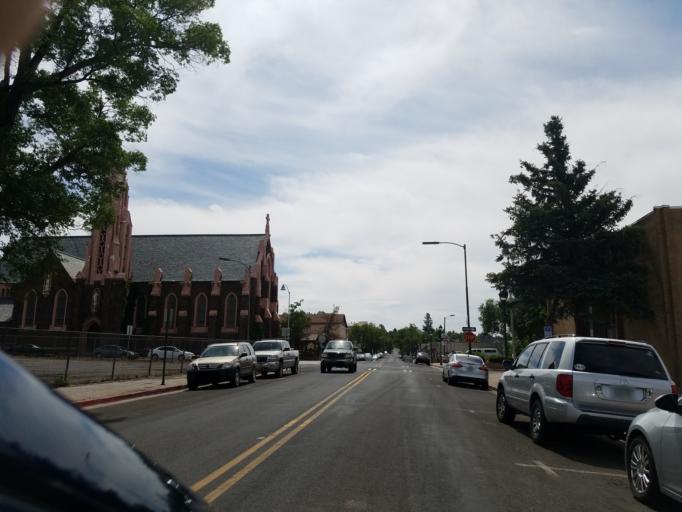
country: US
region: Arizona
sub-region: Coconino County
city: Flagstaff
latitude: 35.2008
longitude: -111.6497
